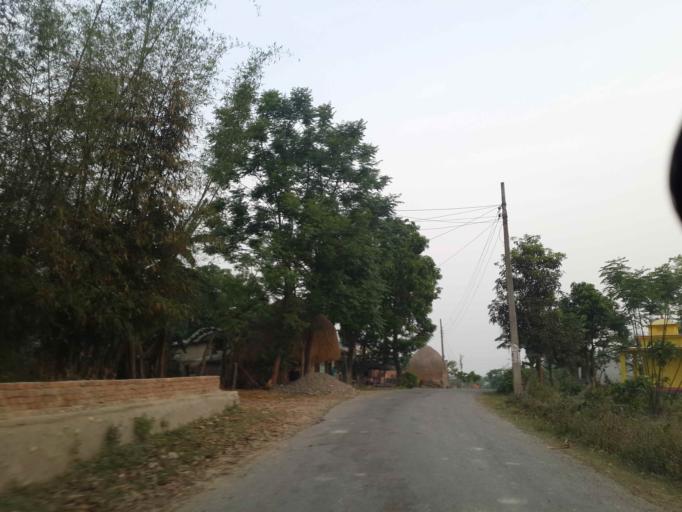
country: NP
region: Central Region
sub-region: Narayani Zone
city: Bharatpur
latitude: 27.5952
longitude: 84.0988
